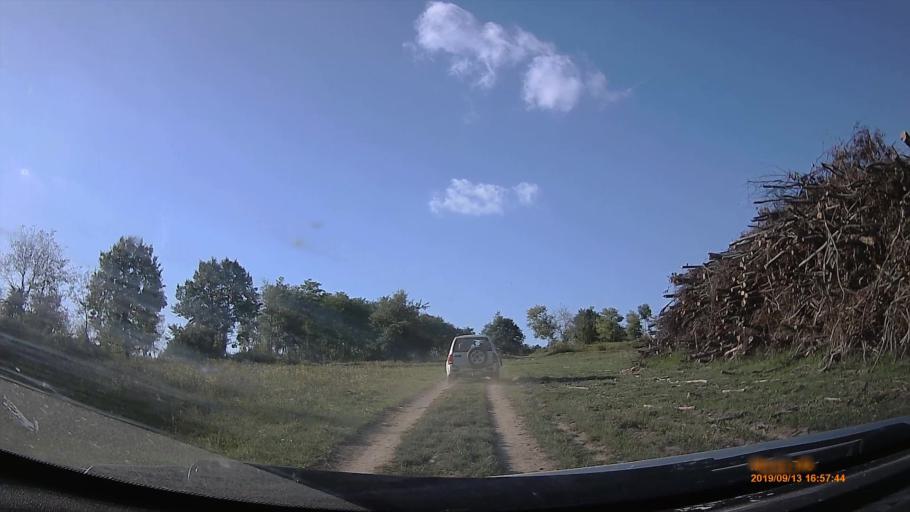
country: HU
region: Zala
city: Pacsa
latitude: 46.5995
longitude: 17.0510
